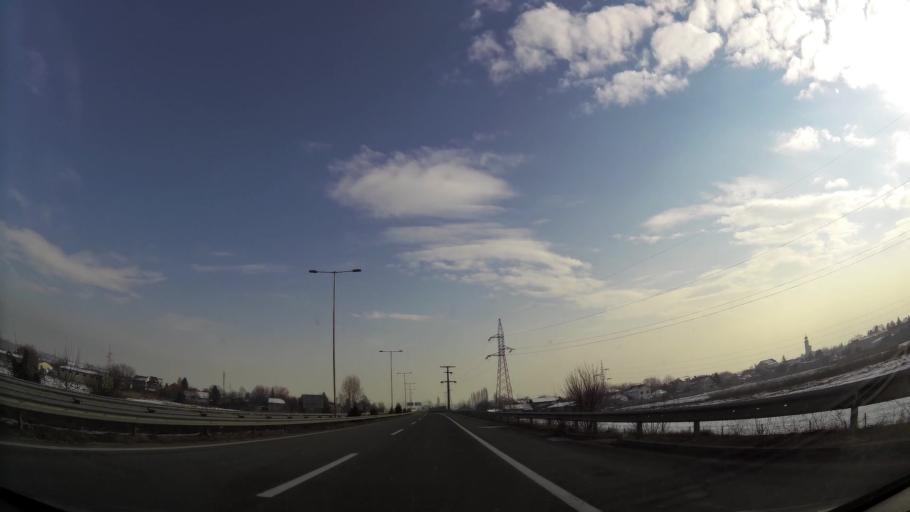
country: MK
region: Butel
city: Butel
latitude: 42.0434
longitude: 21.4461
